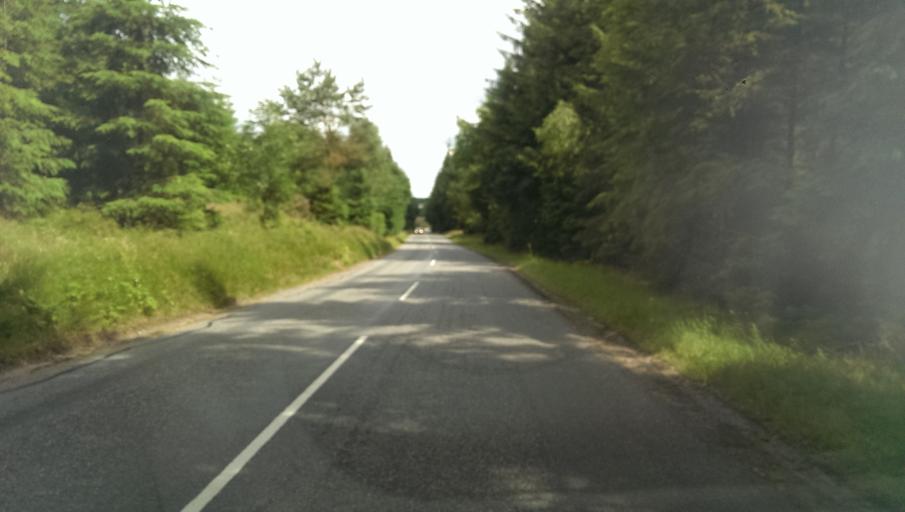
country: DK
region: Central Jutland
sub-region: Silkeborg Kommune
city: Virklund
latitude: 56.0796
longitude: 9.4177
